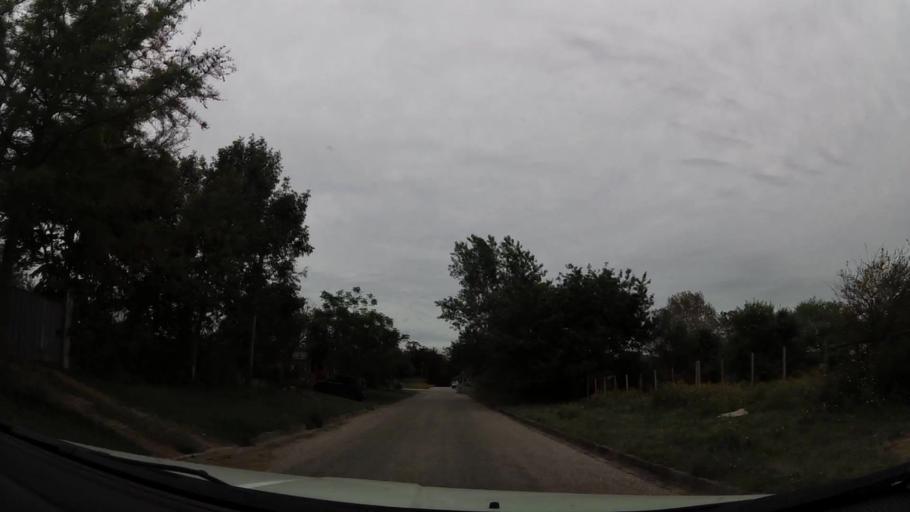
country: UY
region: Maldonado
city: Maldonado
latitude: -34.8812
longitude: -54.9863
